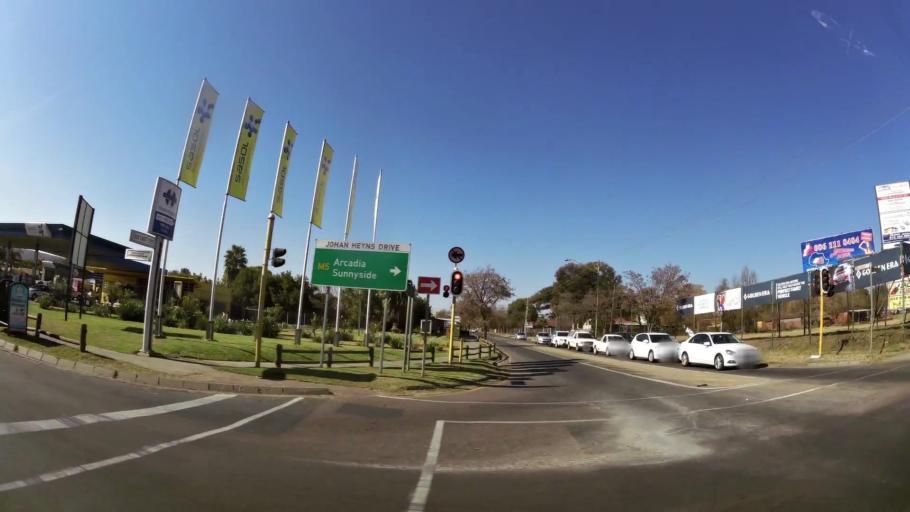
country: ZA
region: Gauteng
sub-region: City of Tshwane Metropolitan Municipality
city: Pretoria
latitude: -25.7142
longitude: 28.2034
